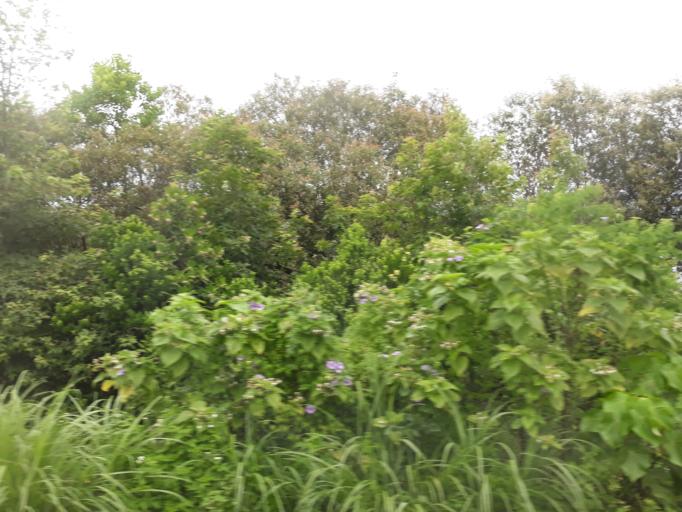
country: TW
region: Taiwan
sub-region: Yilan
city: Yilan
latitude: 24.6843
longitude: 121.7748
